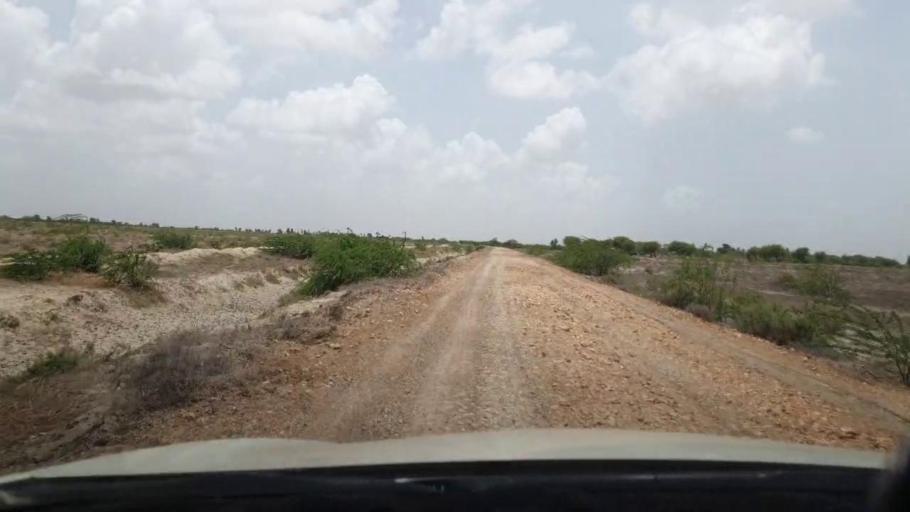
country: PK
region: Sindh
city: Kadhan
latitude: 24.3679
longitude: 68.9271
